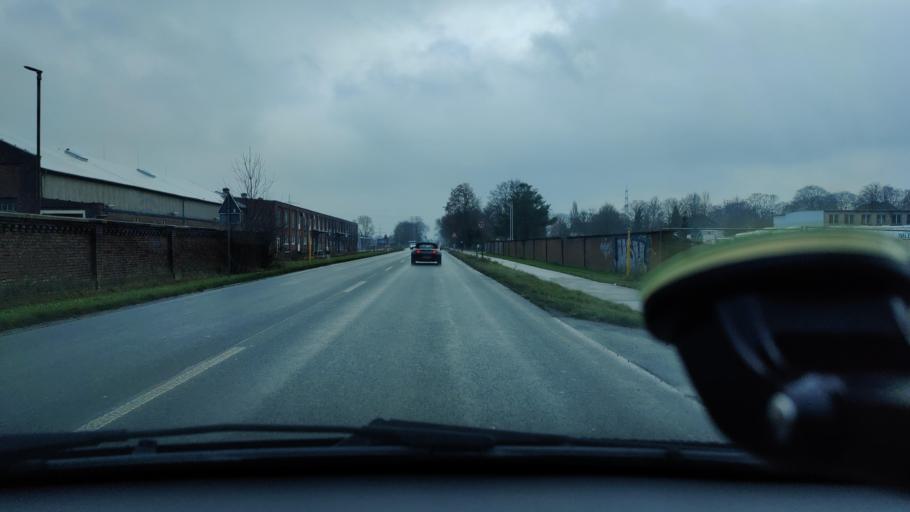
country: DE
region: North Rhine-Westphalia
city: Rheinberg
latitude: 51.5628
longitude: 6.5800
